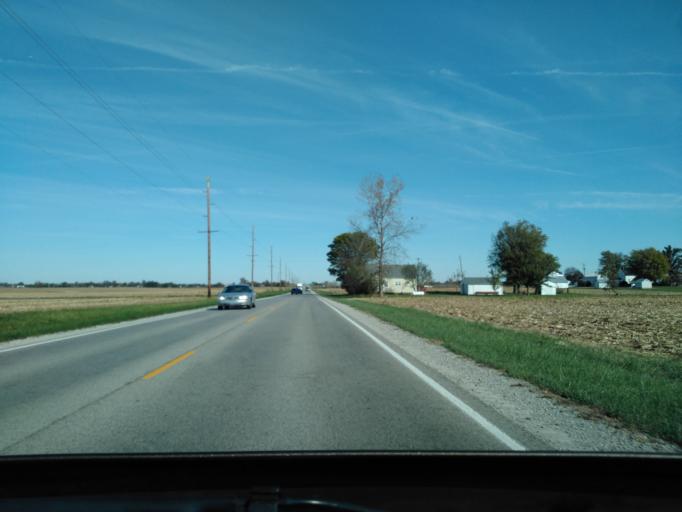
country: US
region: Illinois
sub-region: Madison County
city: Saint Jacob
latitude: 38.7488
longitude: -89.8004
